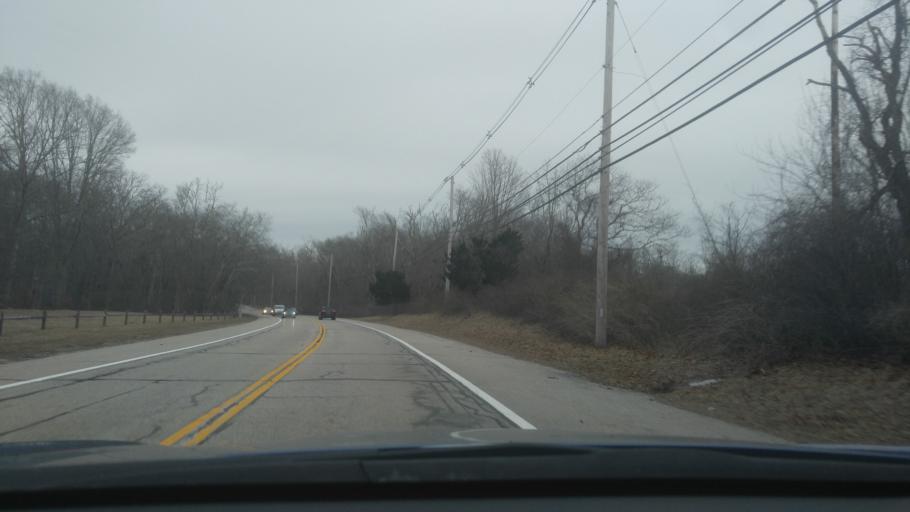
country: US
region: Rhode Island
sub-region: Washington County
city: North Kingstown
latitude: 41.5369
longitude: -71.4375
